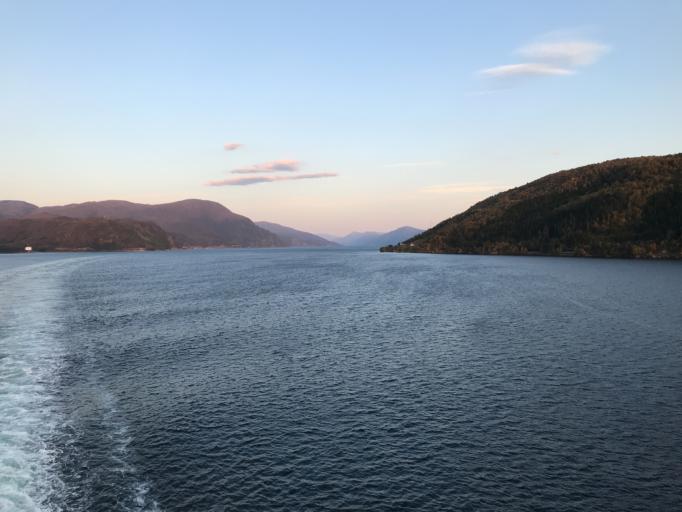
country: NO
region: Sogn og Fjordane
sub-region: Selje
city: Selje
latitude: 61.9197
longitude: 5.4017
